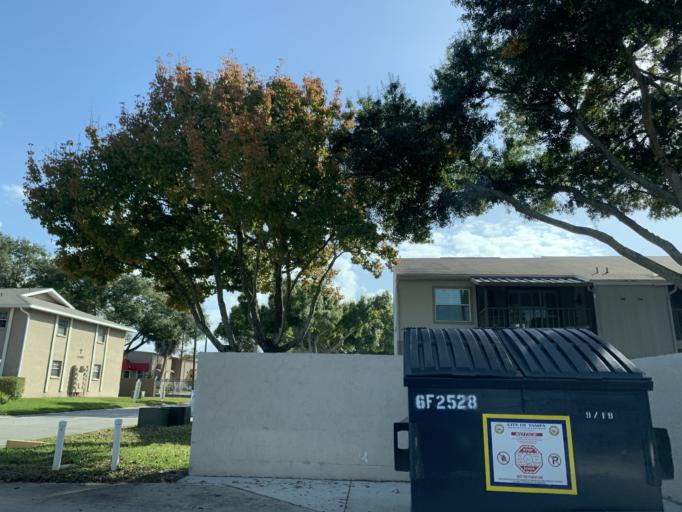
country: US
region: Florida
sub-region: Hillsborough County
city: Tampa
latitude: 27.9015
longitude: -82.5081
